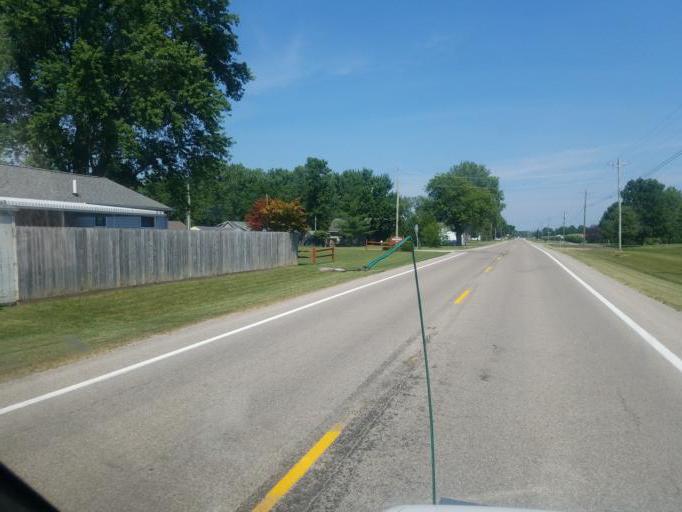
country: US
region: Ohio
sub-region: Mercer County
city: Celina
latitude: 40.5020
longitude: -84.5048
